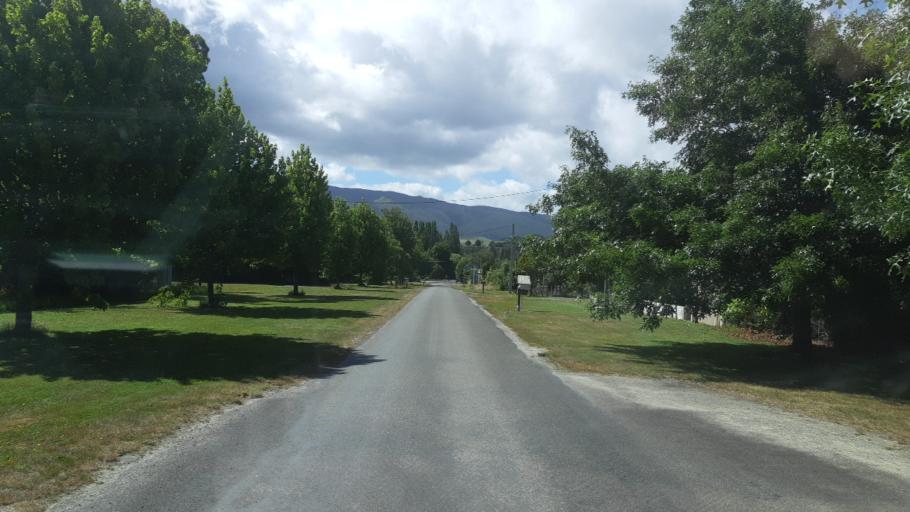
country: NZ
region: Manawatu-Wanganui
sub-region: Palmerston North City
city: Palmerston North
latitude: -40.1714
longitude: 175.7922
